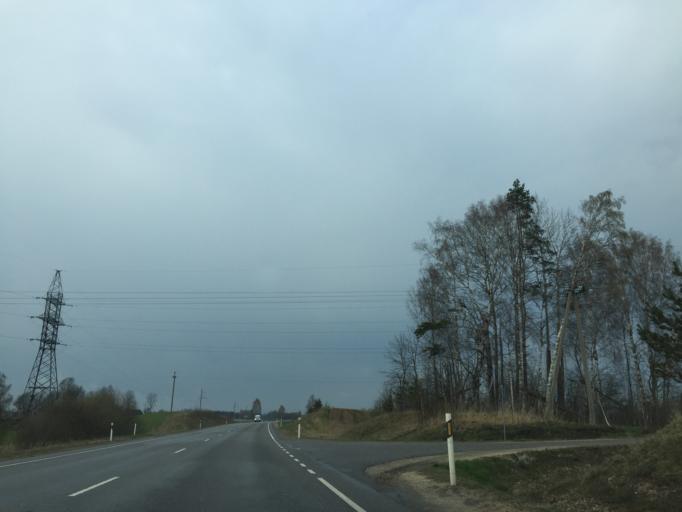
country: EE
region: Tartu
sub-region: UElenurme vald
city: Ulenurme
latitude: 58.1528
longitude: 26.6948
